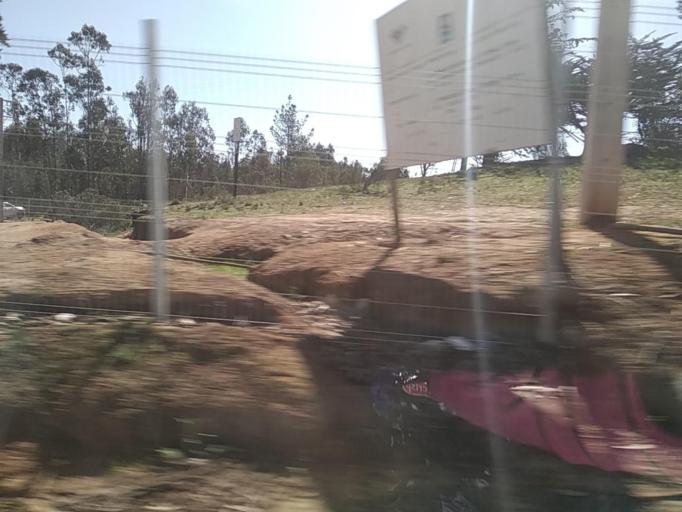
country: CL
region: Valparaiso
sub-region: San Antonio Province
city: El Tabo
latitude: -33.4180
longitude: -71.6236
